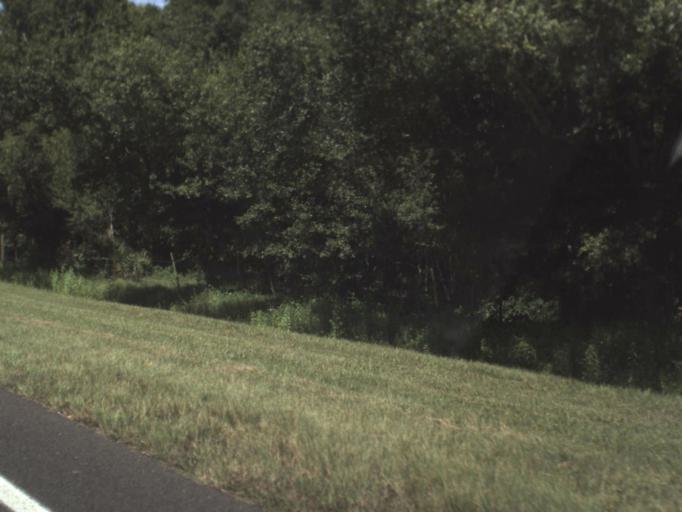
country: US
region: Florida
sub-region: Polk County
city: Fussels Corner
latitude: 28.0491
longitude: -81.8509
